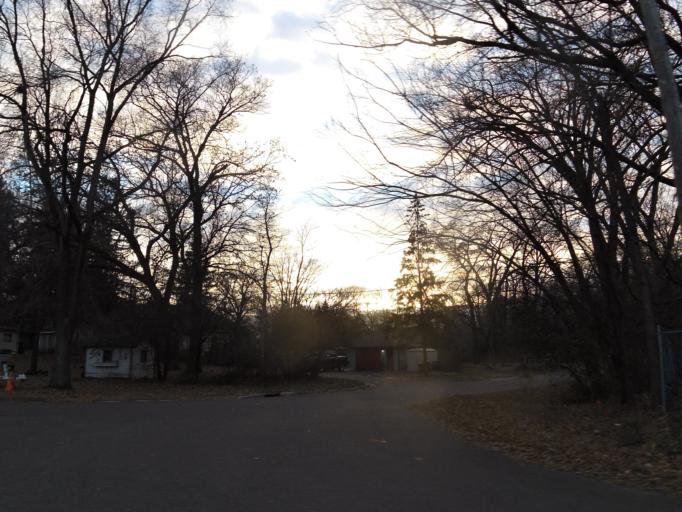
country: US
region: Minnesota
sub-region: Washington County
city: Mahtomedi
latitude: 45.0721
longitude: -92.9565
